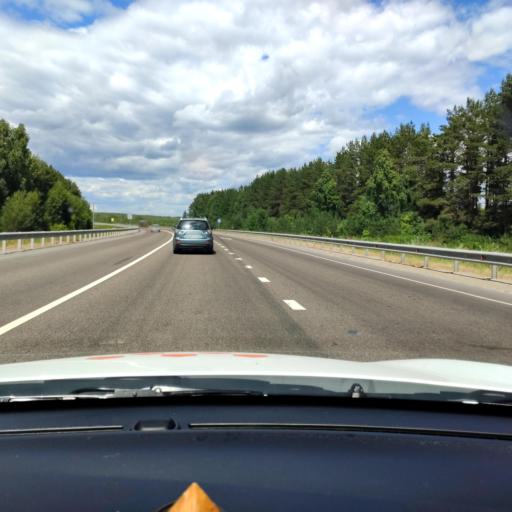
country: RU
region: Mariy-El
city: Pomary
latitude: 55.9224
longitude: 48.3741
